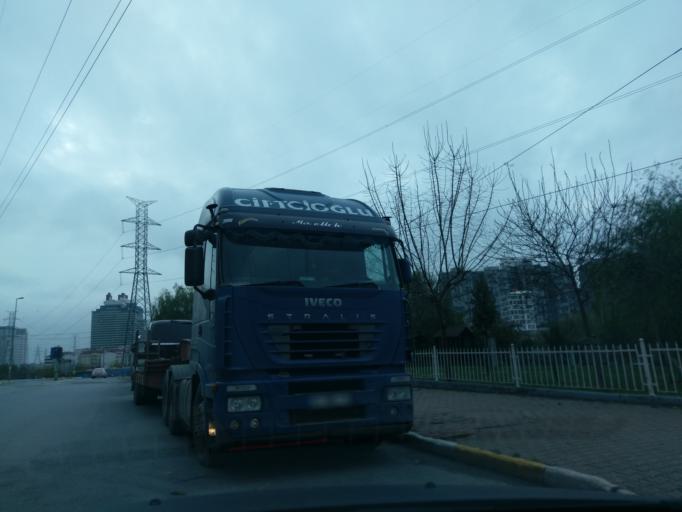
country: TR
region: Istanbul
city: Esenyurt
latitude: 41.0169
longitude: 28.6725
